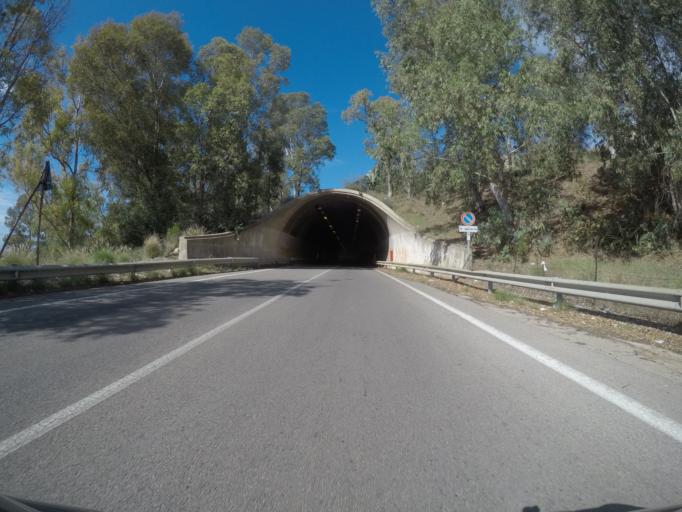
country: IT
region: Sicily
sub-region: Palermo
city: Agliandroni-Paternella
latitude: 38.1232
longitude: 13.0762
